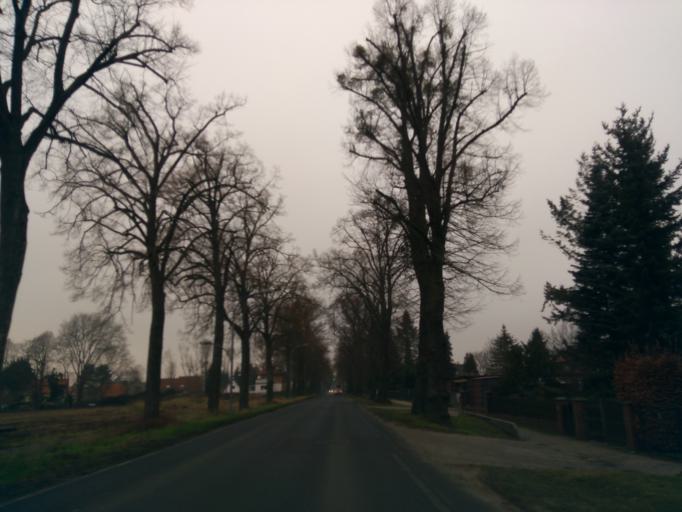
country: DE
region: Brandenburg
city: Dallgow-Doeberitz
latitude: 52.5466
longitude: 13.0625
